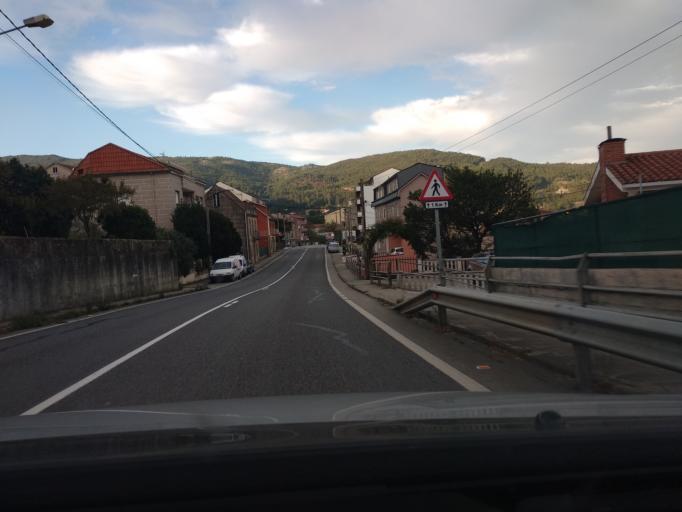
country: ES
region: Galicia
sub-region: Provincia de Pontevedra
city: Vigo
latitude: 42.2836
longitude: -8.6850
